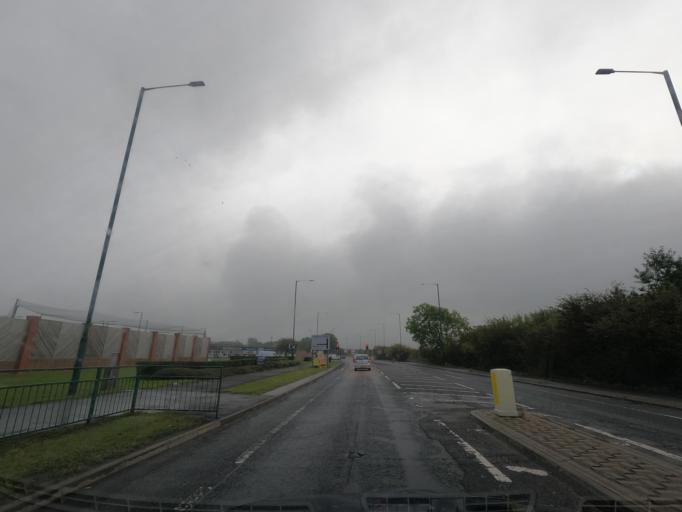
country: GB
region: England
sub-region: Redcar and Cleveland
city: South Bank
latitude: 54.5691
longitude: -1.1780
